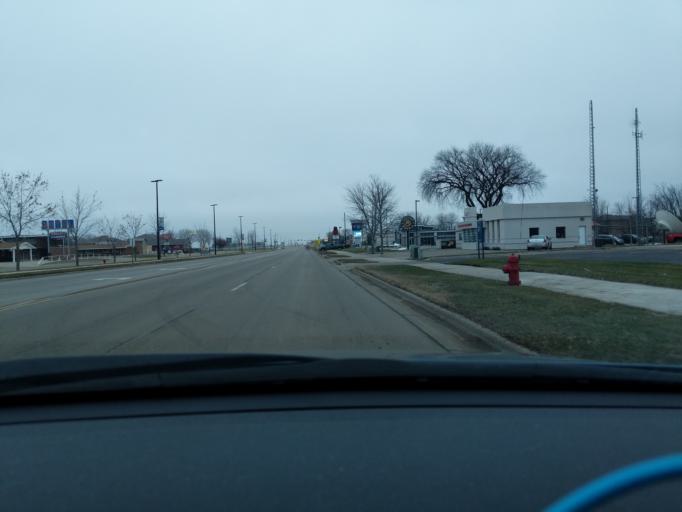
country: US
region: Minnesota
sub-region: Lyon County
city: Marshall
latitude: 44.4504
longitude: -95.7634
